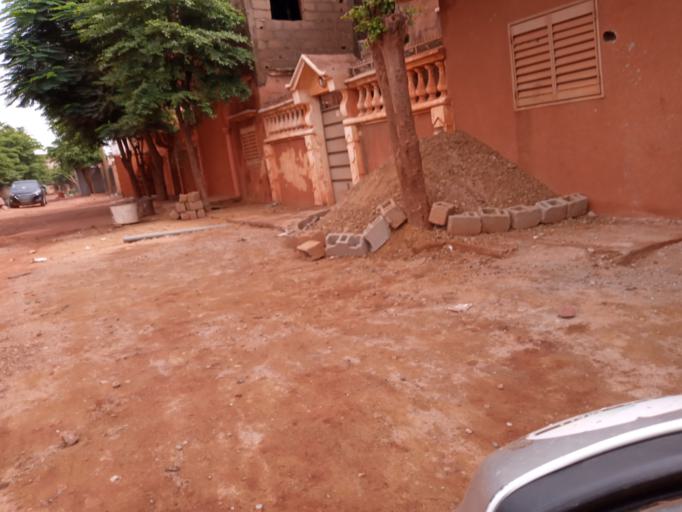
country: ML
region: Bamako
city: Bamako
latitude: 12.5487
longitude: -7.9975
